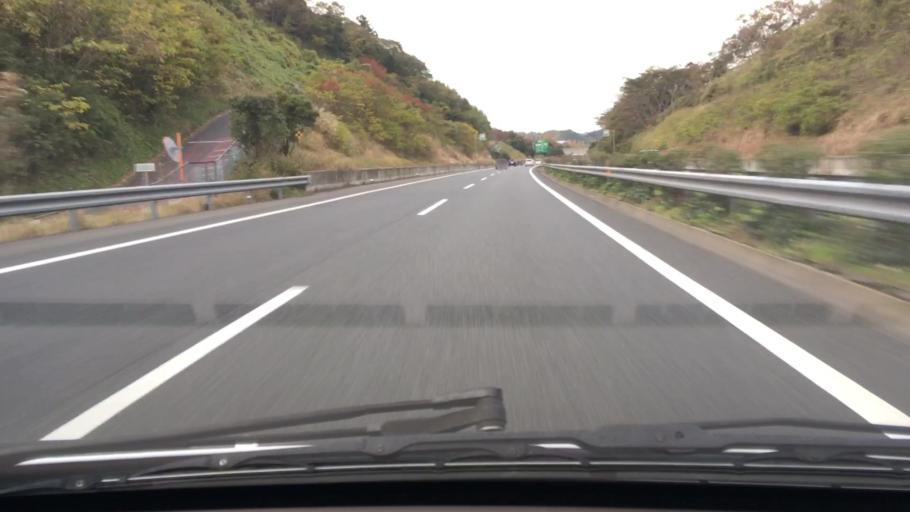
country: JP
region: Chiba
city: Kisarazu
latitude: 35.3349
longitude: 139.9449
